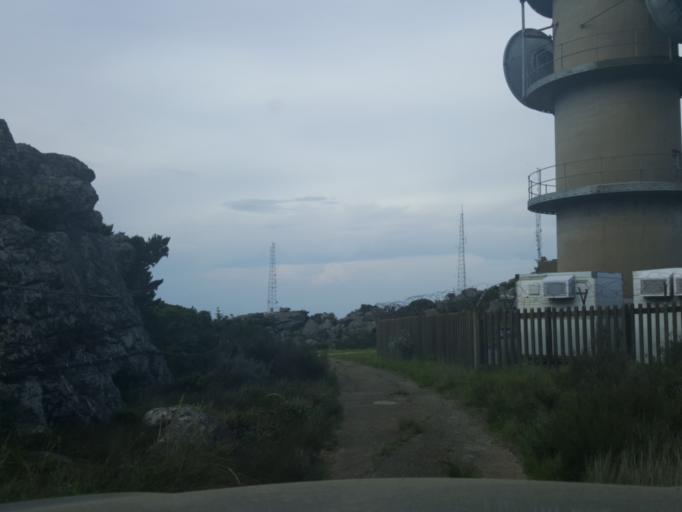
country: ZA
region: Limpopo
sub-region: Mopani District Municipality
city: Hoedspruit
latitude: -24.5402
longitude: 30.8703
